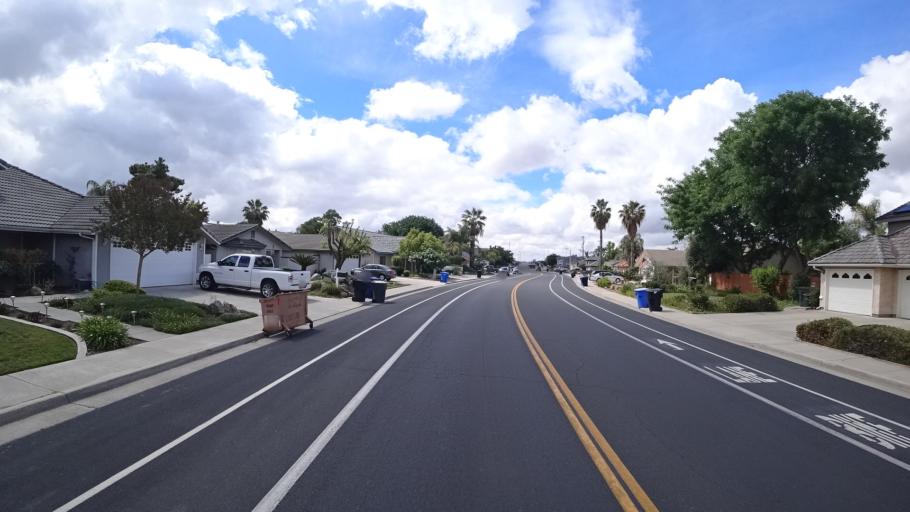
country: US
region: California
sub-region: Kings County
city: Hanford
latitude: 36.3379
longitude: -119.6657
